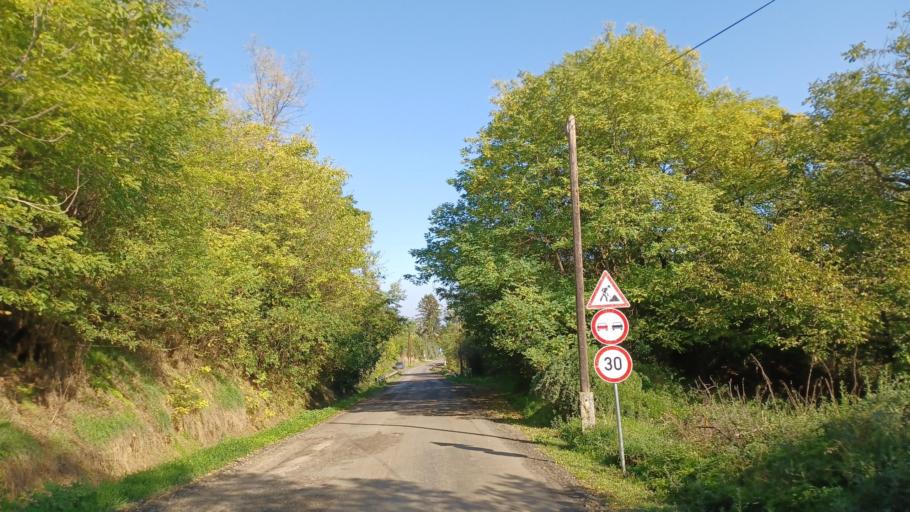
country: HU
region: Tolna
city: Nagydorog
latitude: 46.5477
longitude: 18.5909
